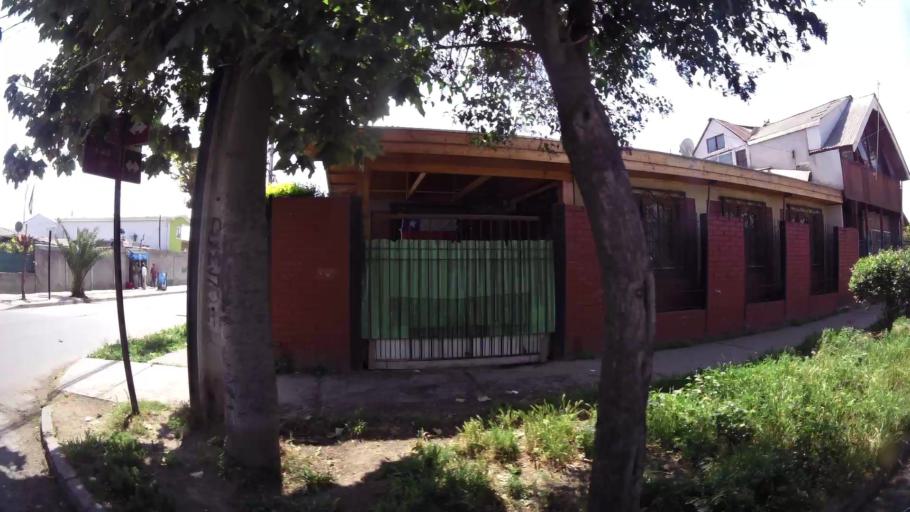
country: CL
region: Santiago Metropolitan
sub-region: Provincia de Santiago
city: Lo Prado
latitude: -33.4273
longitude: -70.7259
